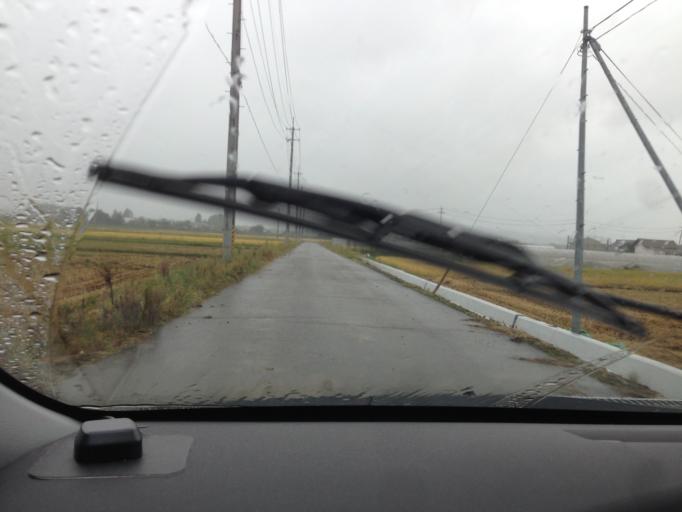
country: JP
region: Fukushima
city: Kitakata
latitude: 37.4615
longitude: 139.8670
